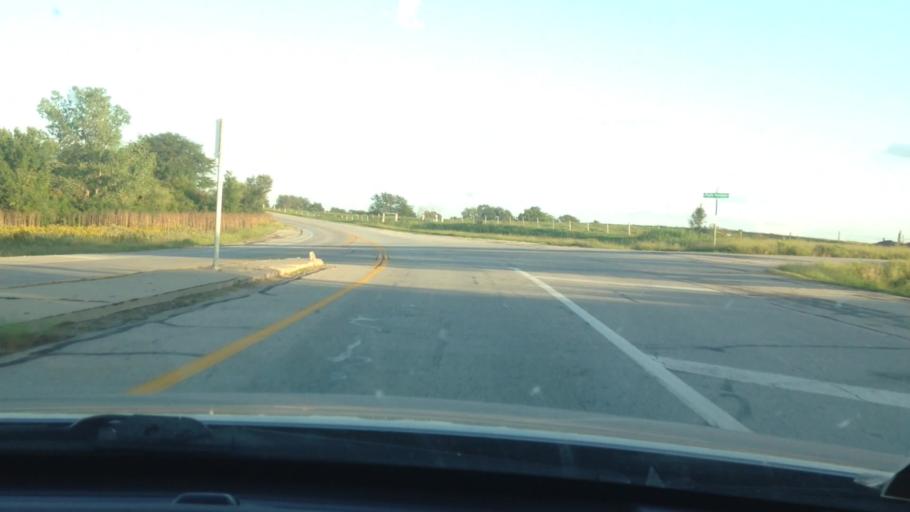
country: US
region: Missouri
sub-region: Clay County
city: Smithville
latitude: 39.3051
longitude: -94.6004
